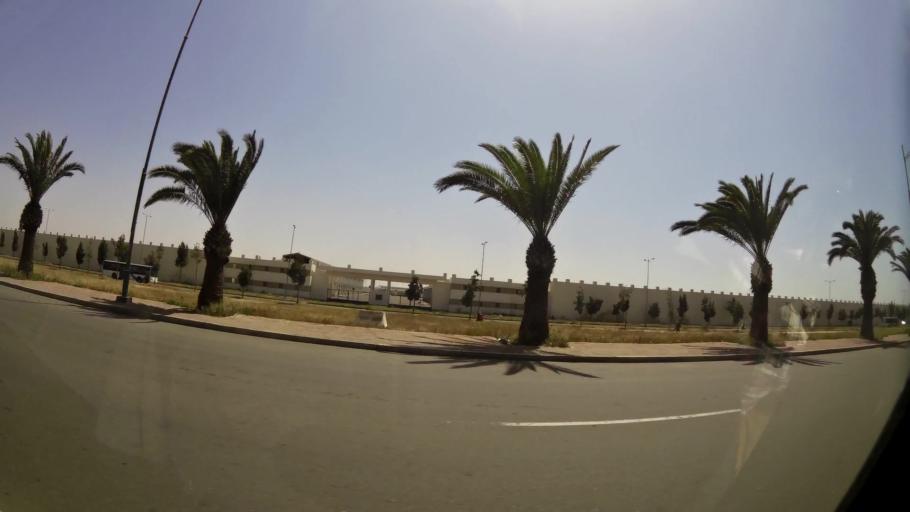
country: MA
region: Souss-Massa-Draa
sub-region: Inezgane-Ait Mellou
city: Inezgane
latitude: 30.3584
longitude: -9.5210
